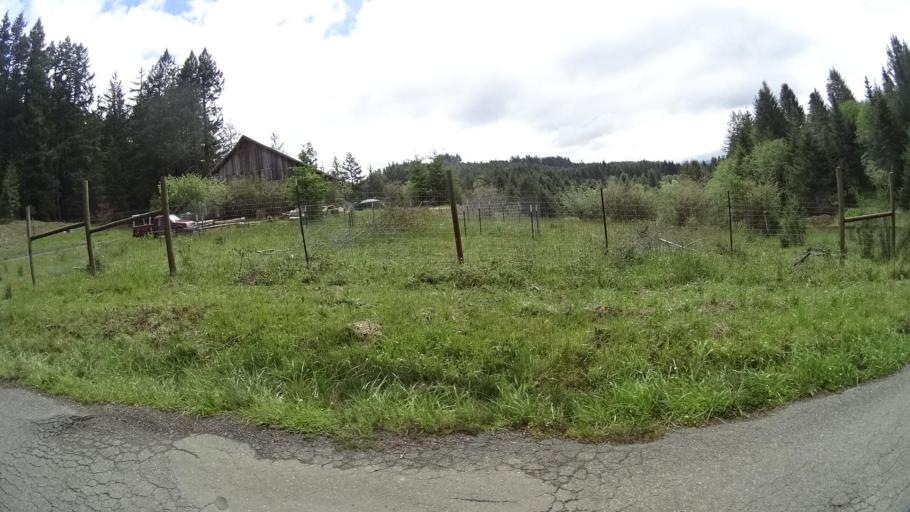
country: US
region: California
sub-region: Humboldt County
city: Bayside
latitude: 40.8385
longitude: -124.0233
